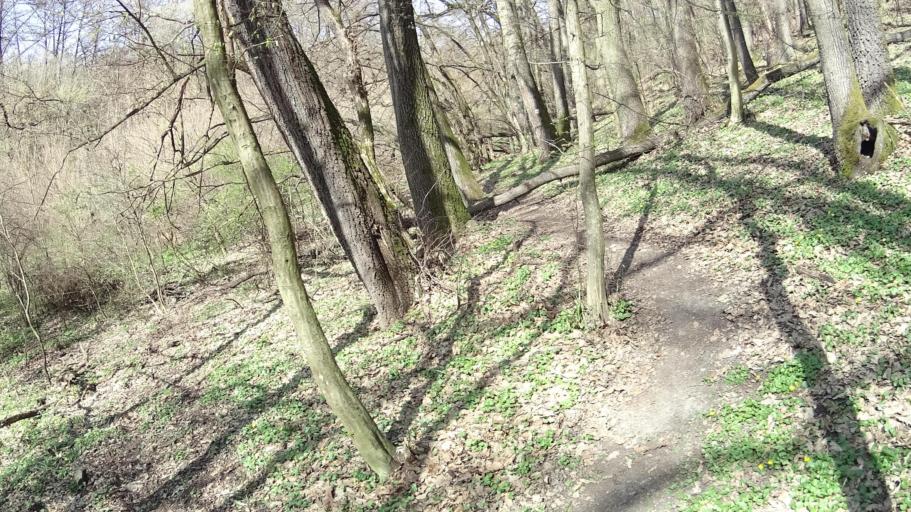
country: HU
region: Pest
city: Veroce
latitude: 47.8594
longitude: 19.0377
